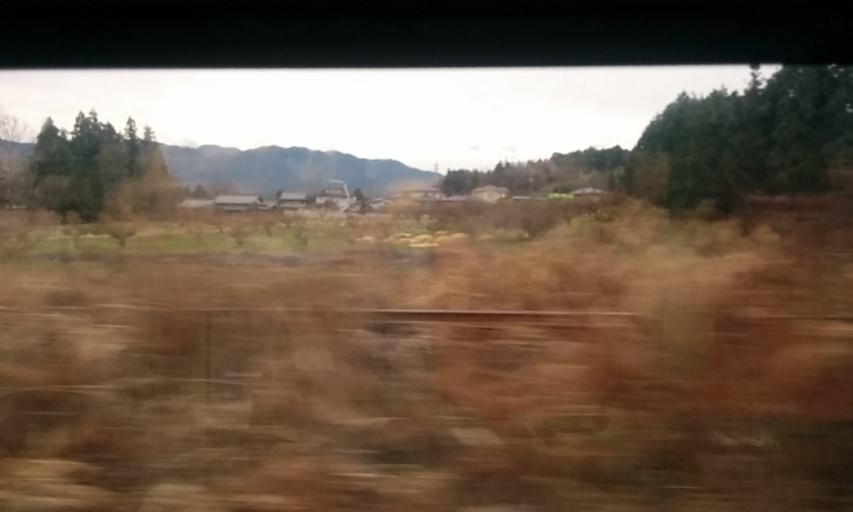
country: JP
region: Gifu
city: Nakatsugawa
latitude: 35.4690
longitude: 137.4181
